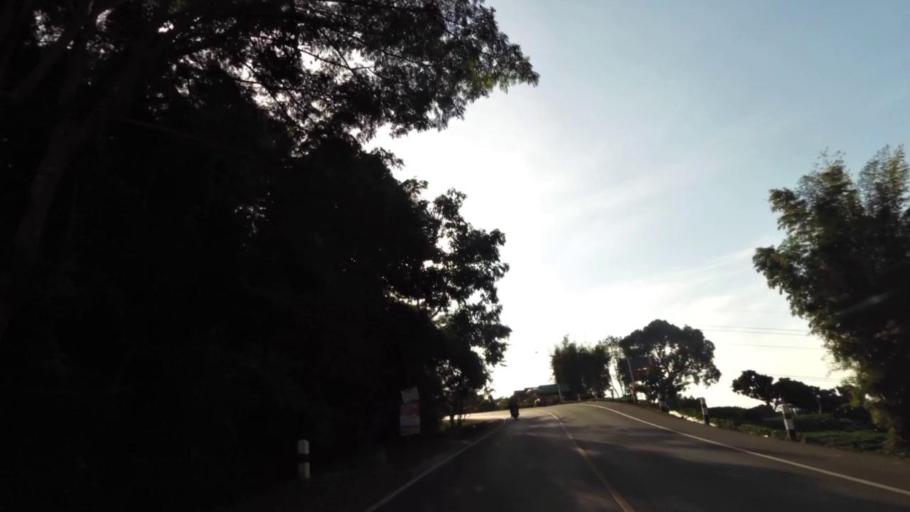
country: TH
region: Chiang Rai
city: Khun Tan
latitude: 19.8601
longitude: 100.4299
